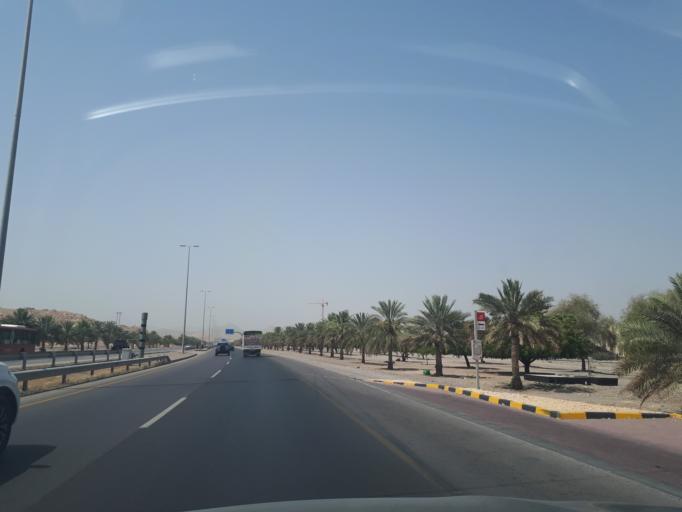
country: OM
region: Muhafazat Masqat
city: As Sib al Jadidah
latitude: 23.5860
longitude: 58.1980
